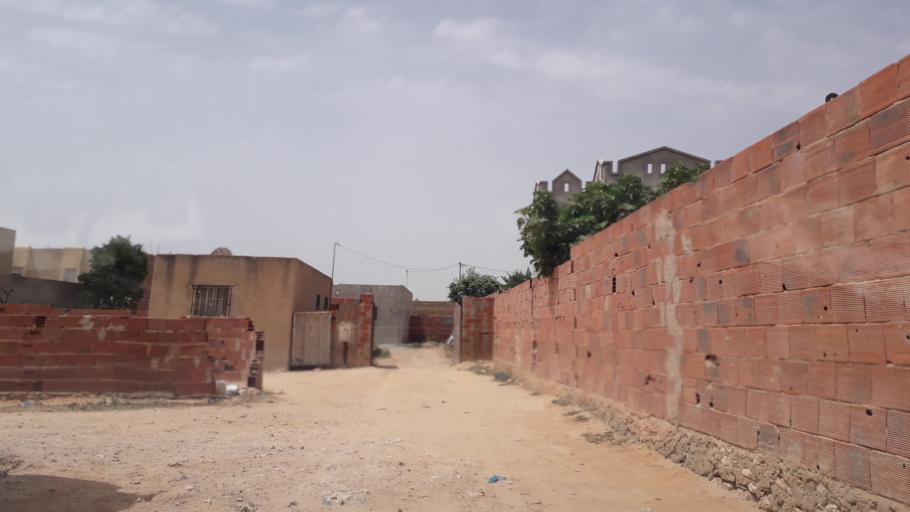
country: TN
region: Safaqis
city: Al Qarmadah
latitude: 34.8402
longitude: 10.7753
